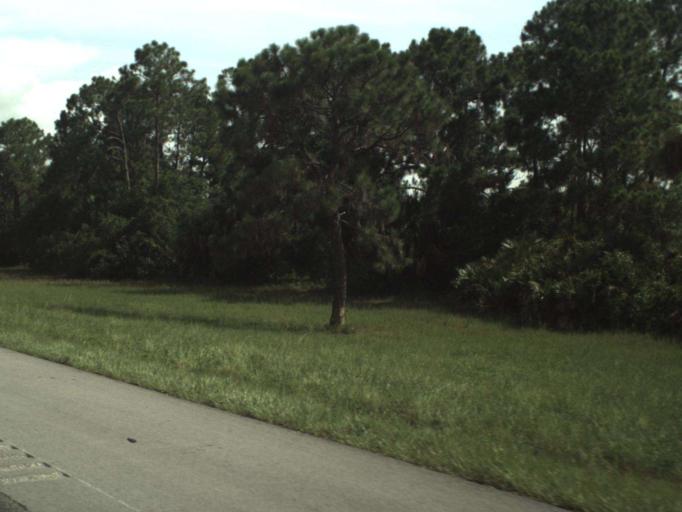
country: US
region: Florida
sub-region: Saint Lucie County
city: Lakewood Park
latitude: 27.4869
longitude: -80.4362
